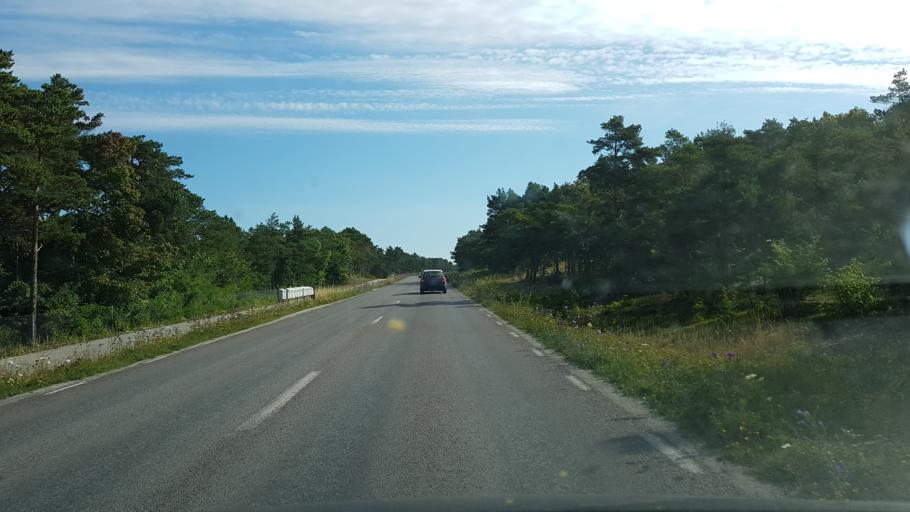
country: SE
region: Gotland
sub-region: Gotland
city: Visby
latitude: 57.7170
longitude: 18.3891
